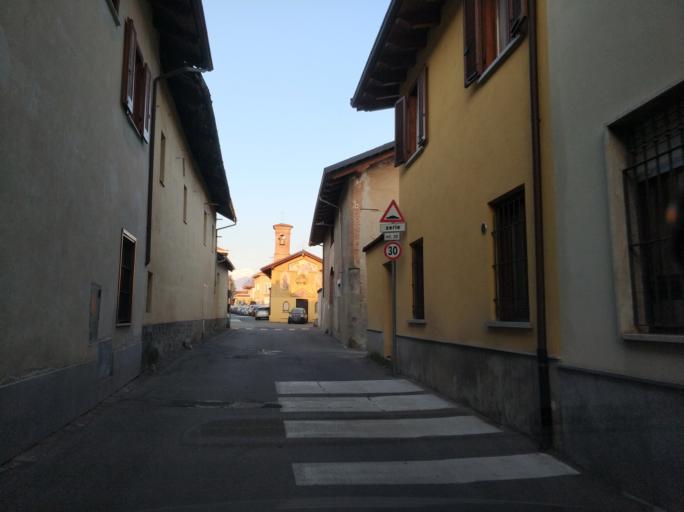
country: IT
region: Piedmont
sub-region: Provincia di Torino
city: Nole
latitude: 45.2456
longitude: 7.5708
